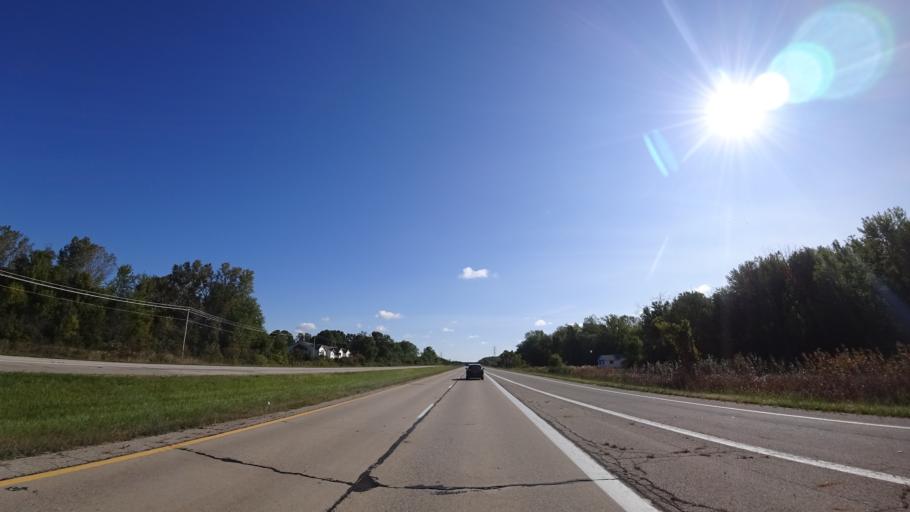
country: US
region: Michigan
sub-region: Berrien County
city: Benton Heights
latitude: 42.1191
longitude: -86.4147
